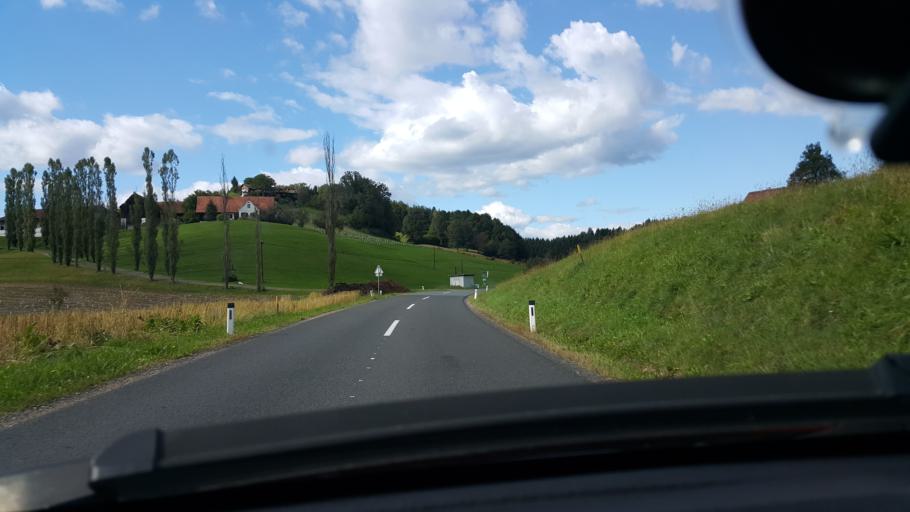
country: AT
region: Styria
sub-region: Politischer Bezirk Deutschlandsberg
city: Wies
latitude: 46.7125
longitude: 15.3054
